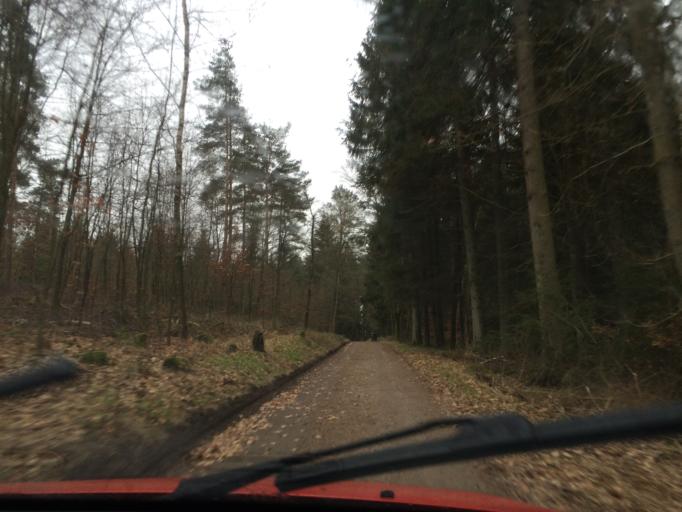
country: DK
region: Central Jutland
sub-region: Silkeborg Kommune
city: Virklund
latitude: 56.0299
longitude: 9.4925
